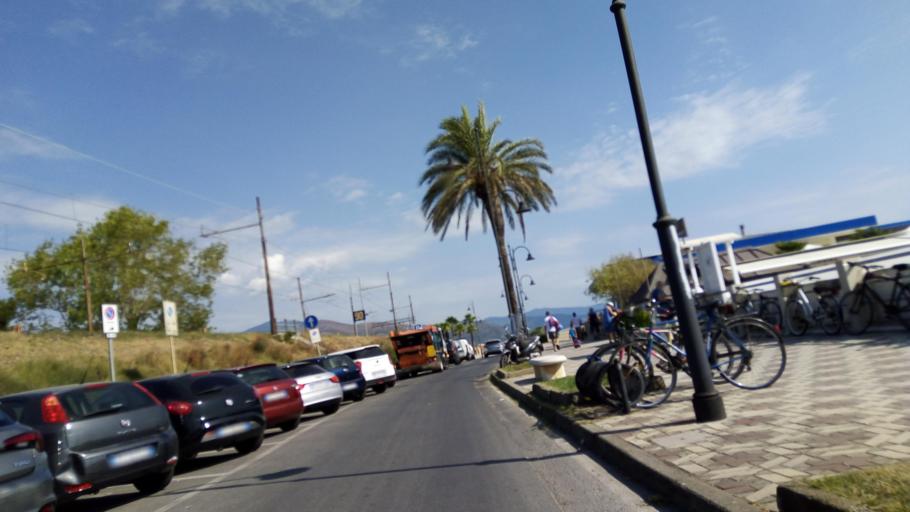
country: IT
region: Liguria
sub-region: Provincia di Savona
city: Albenga
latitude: 44.0523
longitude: 8.2257
